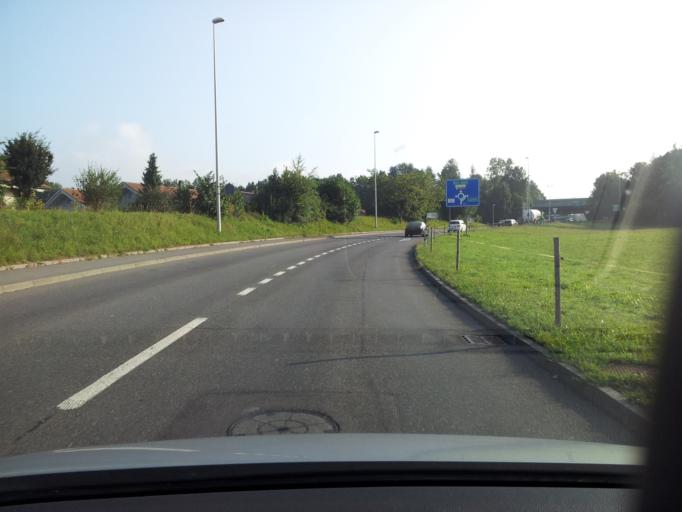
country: CH
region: Lucerne
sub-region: Sursee District
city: Sempach
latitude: 47.1352
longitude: 8.1966
